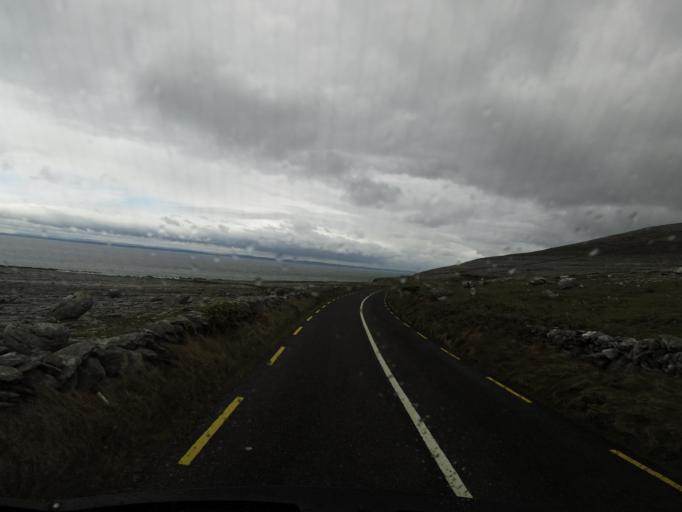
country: IE
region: Connaught
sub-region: County Galway
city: Bearna
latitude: 53.1429
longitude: -9.2743
